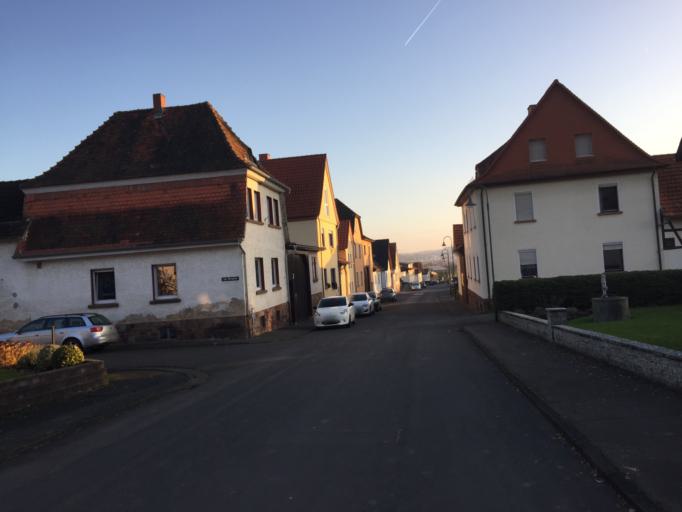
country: DE
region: Hesse
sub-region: Regierungsbezirk Darmstadt
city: Munzenberg
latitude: 50.4813
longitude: 8.7612
